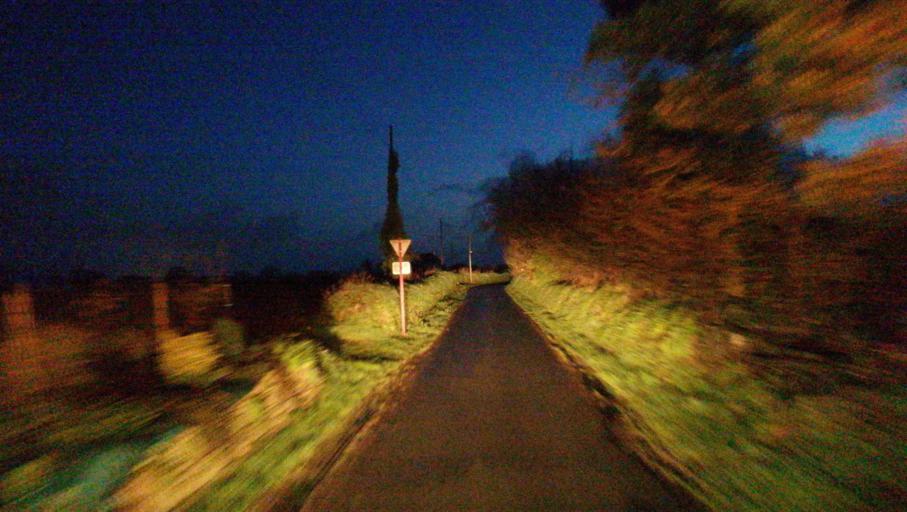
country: FR
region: Brittany
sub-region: Departement des Cotes-d'Armor
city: Pommerit-le-Vicomte
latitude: 48.6568
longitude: -3.0578
